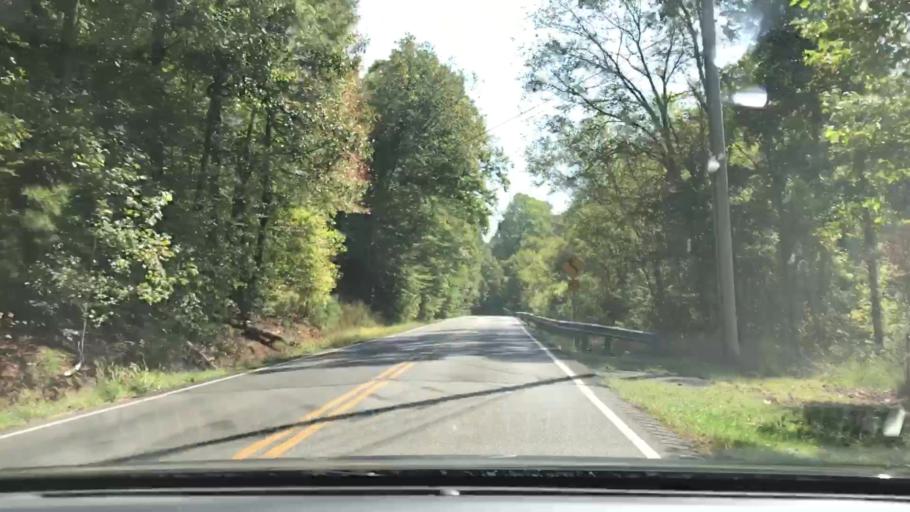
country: US
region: Kentucky
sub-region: Marshall County
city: Benton
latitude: 36.7671
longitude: -88.2733
